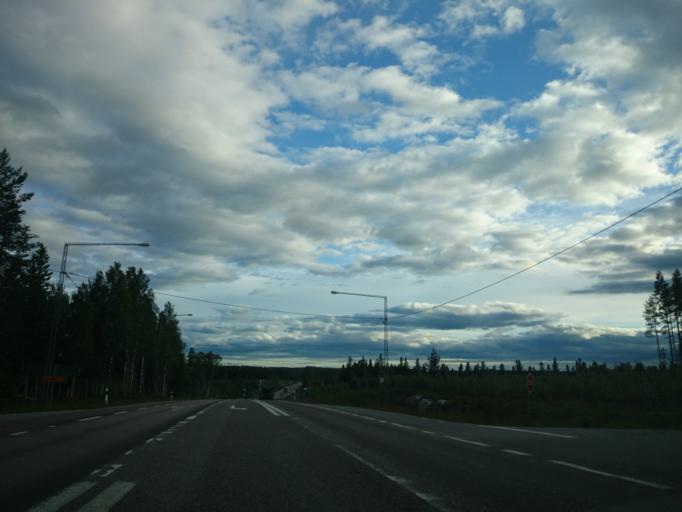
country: SE
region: Vaesternorrland
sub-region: Haernoesands Kommun
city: Haernoesand
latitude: 62.5986
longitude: 17.8088
